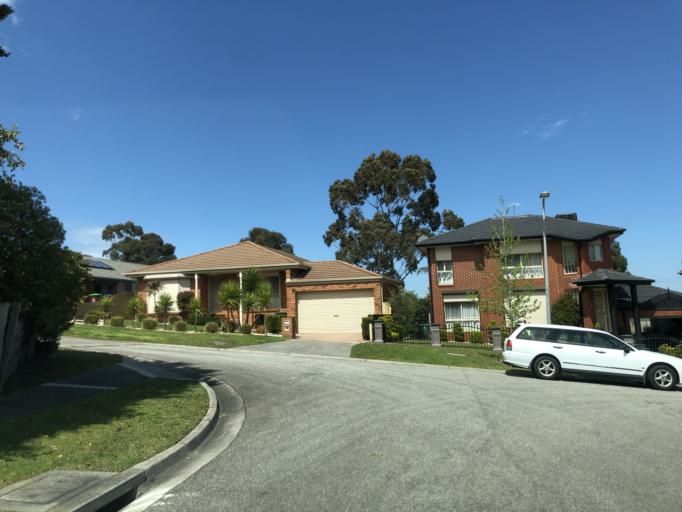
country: AU
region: Victoria
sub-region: Casey
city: Endeavour Hills
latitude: -37.9692
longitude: 145.2785
